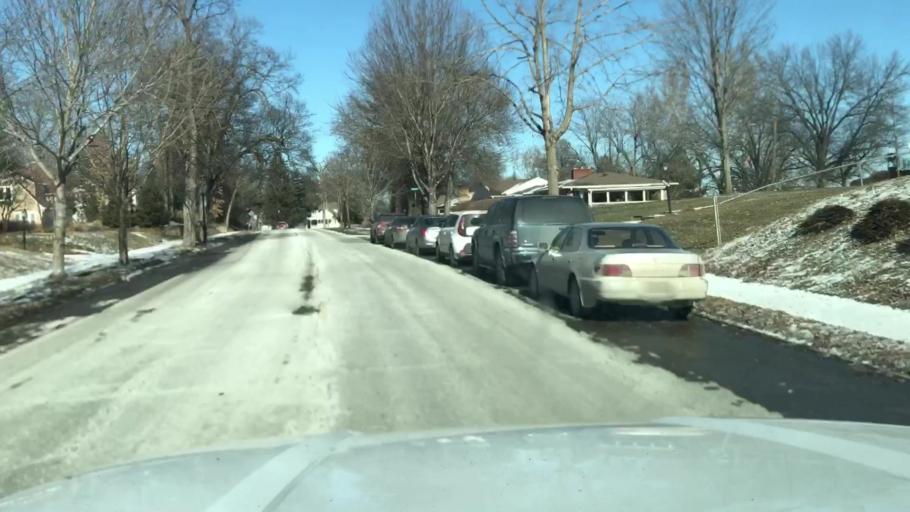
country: US
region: Missouri
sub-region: Andrew County
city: Country Club Village
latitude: 39.7961
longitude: -94.8192
